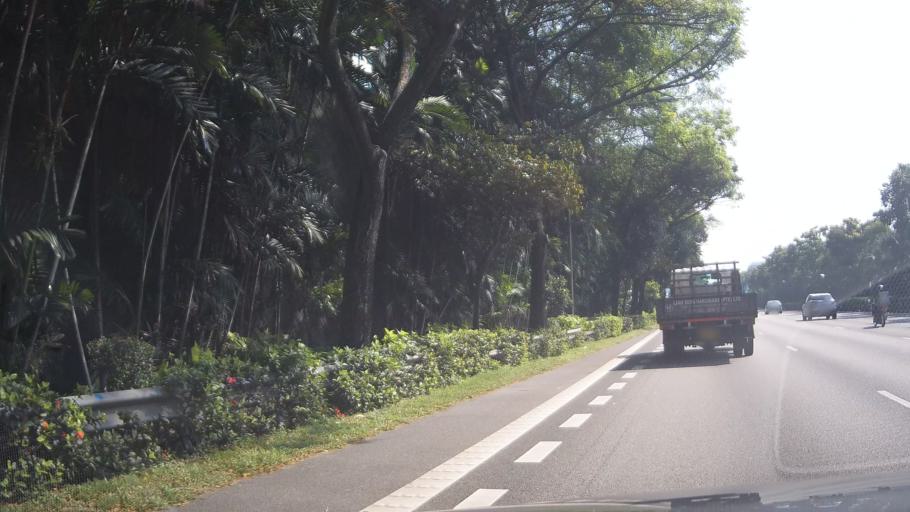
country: MY
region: Johor
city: Johor Bahru
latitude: 1.3439
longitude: 103.6875
